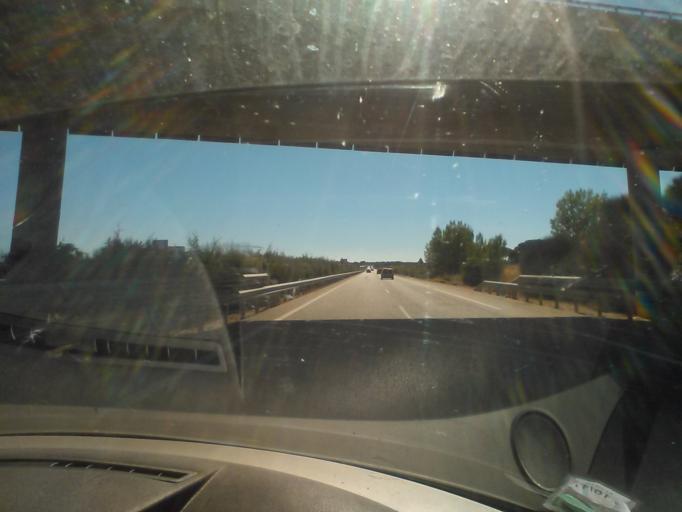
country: ES
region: Castille and Leon
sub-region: Provincia de Zamora
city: Quintanilla de Urz
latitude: 42.0209
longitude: -5.8513
